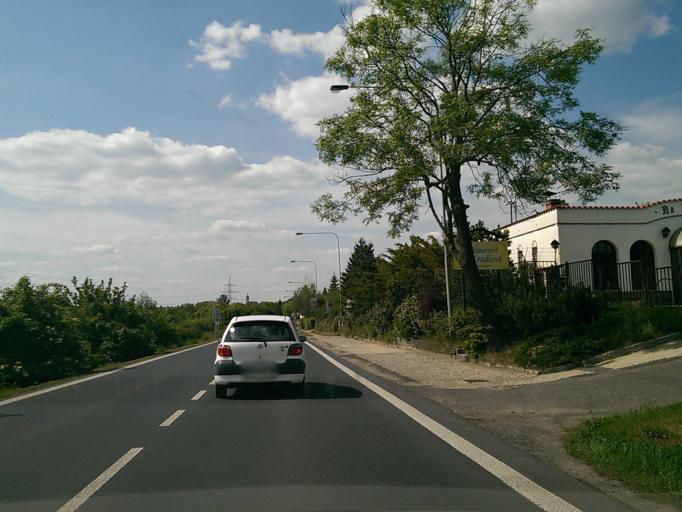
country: CZ
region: Central Bohemia
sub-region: Okres Melnik
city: Melnik
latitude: 50.3308
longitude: 14.4993
